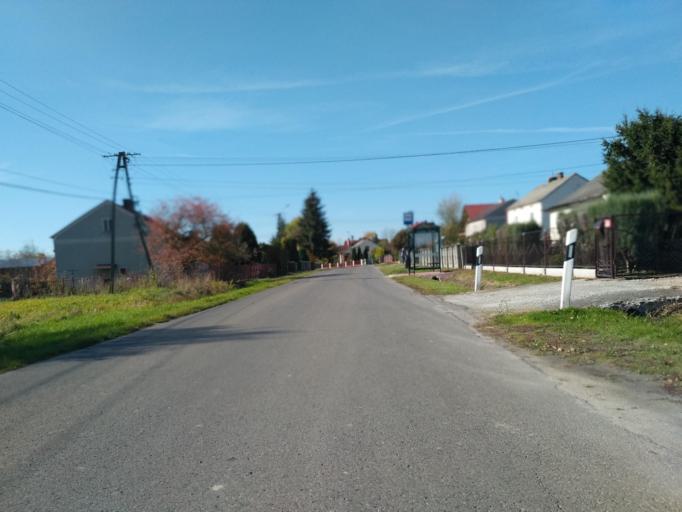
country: PL
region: Subcarpathian Voivodeship
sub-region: Powiat rzeszowski
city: Trzciana
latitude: 50.0808
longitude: 21.8065
